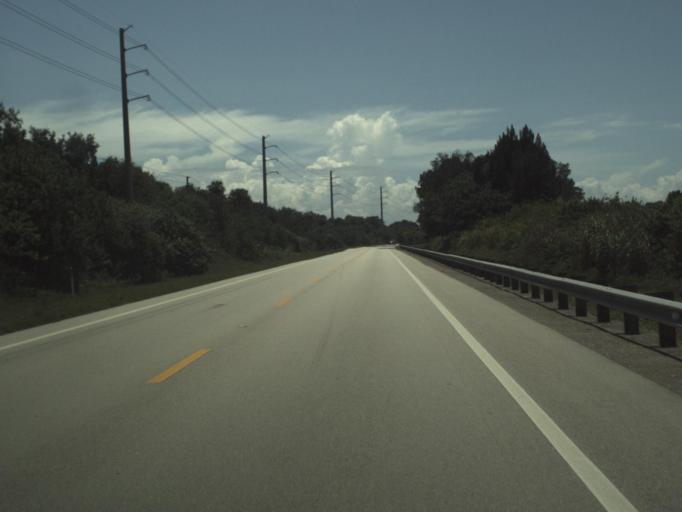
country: US
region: Florida
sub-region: Martin County
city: Indiantown
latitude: 27.0165
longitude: -80.4428
